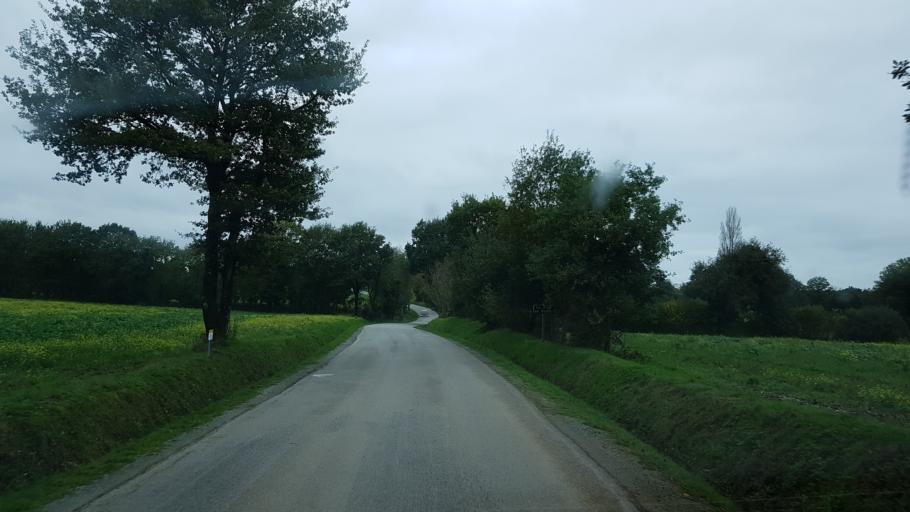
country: FR
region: Brittany
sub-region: Departement du Morbihan
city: Serent
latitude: 47.7805
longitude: -2.4791
